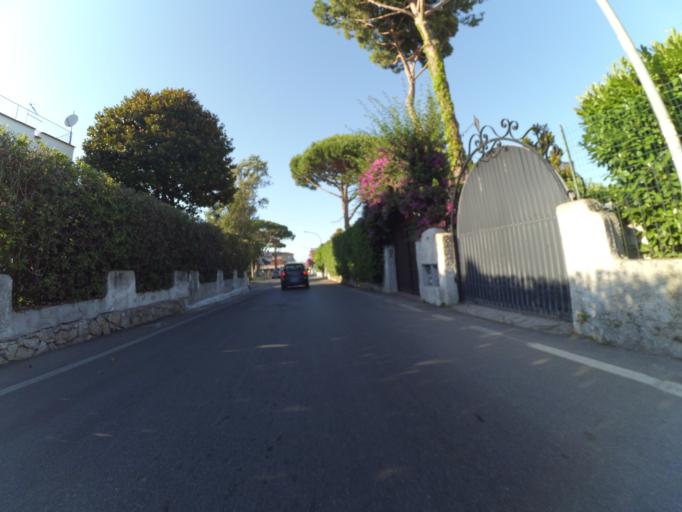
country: IT
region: Latium
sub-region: Provincia di Latina
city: San Felice Circeo
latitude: 41.2406
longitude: 13.0944
